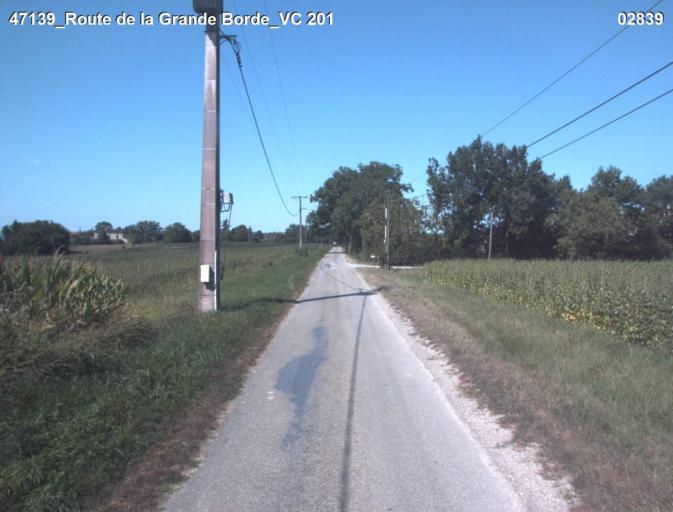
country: FR
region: Aquitaine
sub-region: Departement du Lot-et-Garonne
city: Nerac
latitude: 44.0844
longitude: 0.3815
